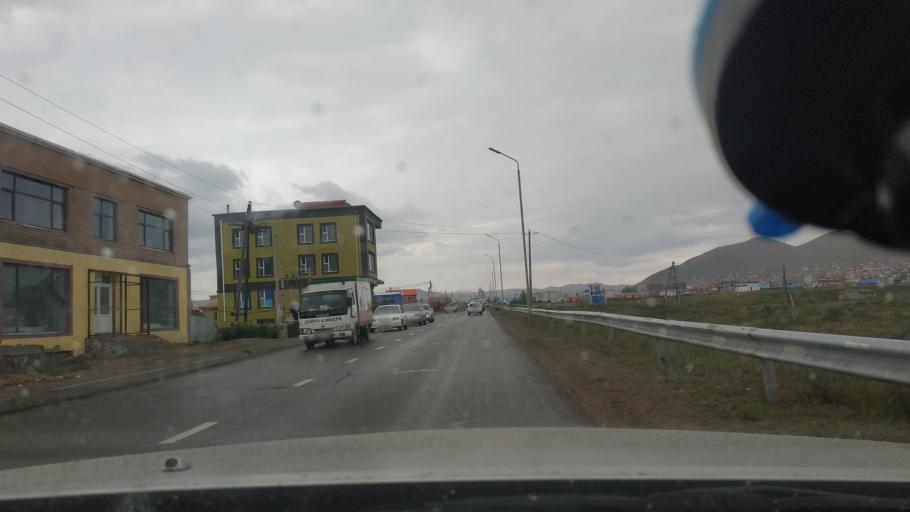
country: MN
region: Ulaanbaatar
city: Ulaanbaatar
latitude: 47.9045
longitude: 107.0350
